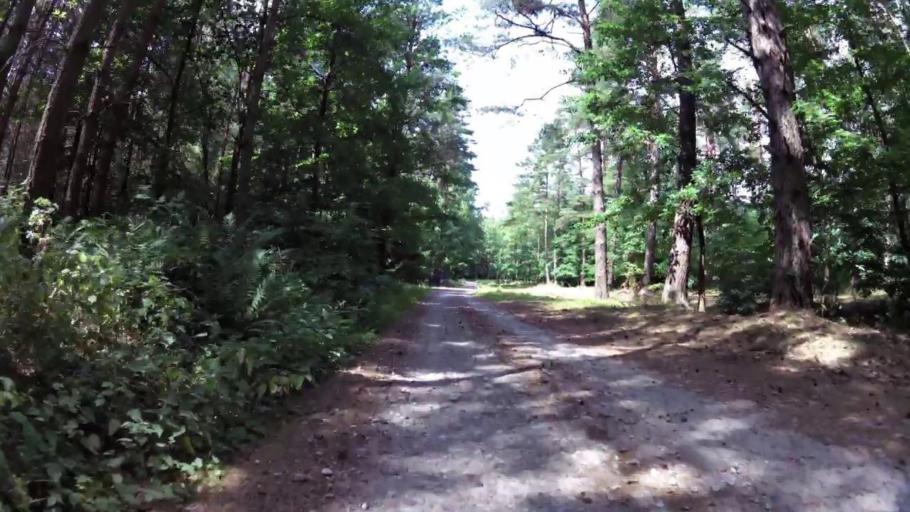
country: PL
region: West Pomeranian Voivodeship
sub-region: Powiat lobeski
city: Lobez
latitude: 53.5672
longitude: 15.6561
